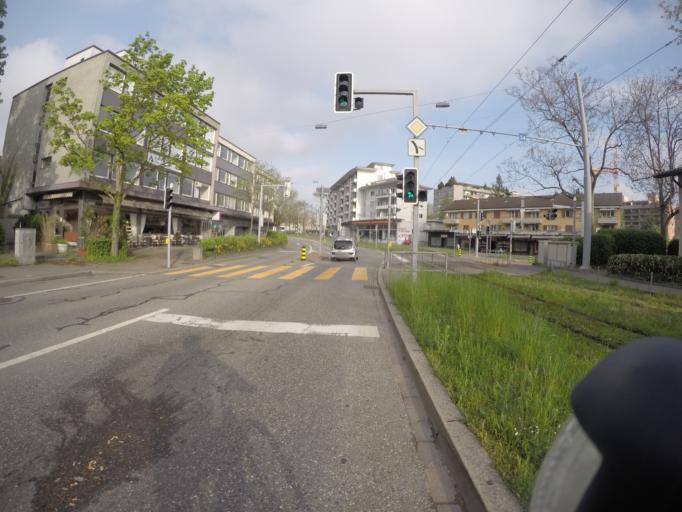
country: CH
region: Zurich
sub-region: Bezirk Zuerich
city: Zuerich (Kreis 12)
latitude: 47.4040
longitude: 8.5744
